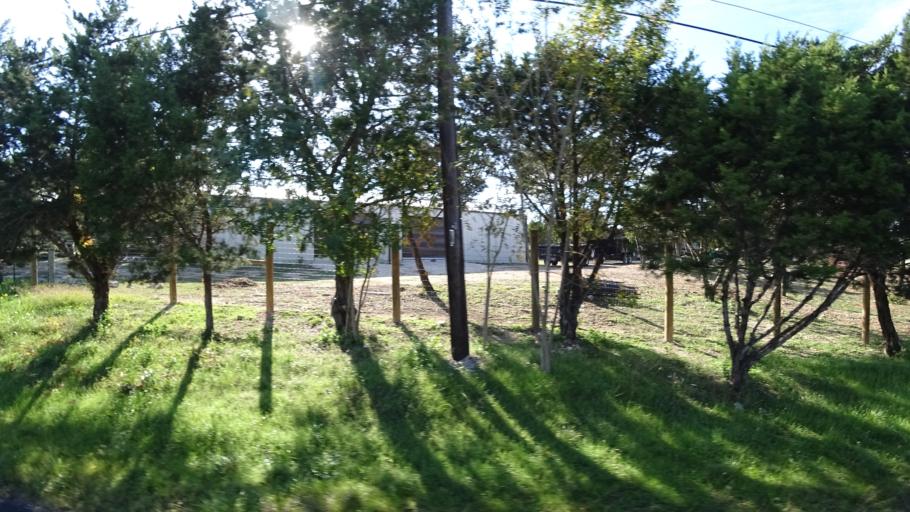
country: US
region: Texas
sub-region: Travis County
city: Bee Cave
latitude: 30.2359
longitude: -97.9382
